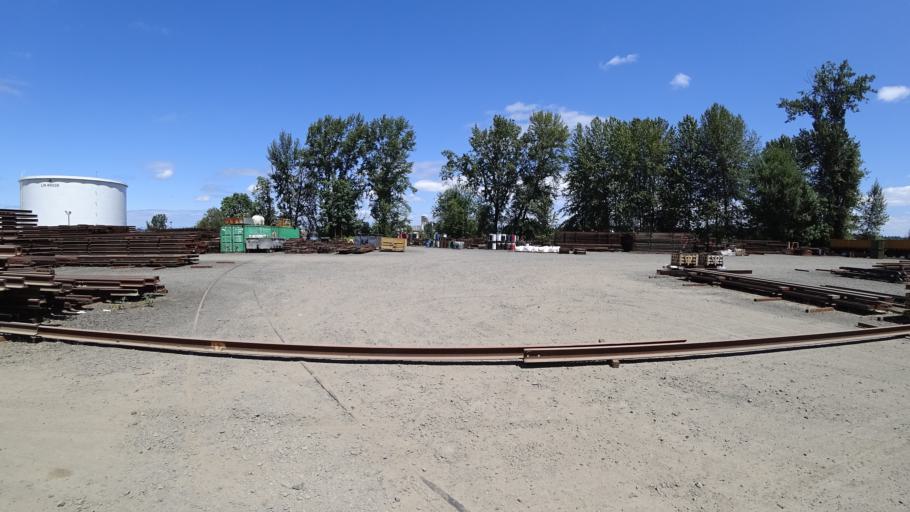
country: US
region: Oregon
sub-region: Washington County
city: Cedar Mill
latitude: 45.6016
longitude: -122.7861
